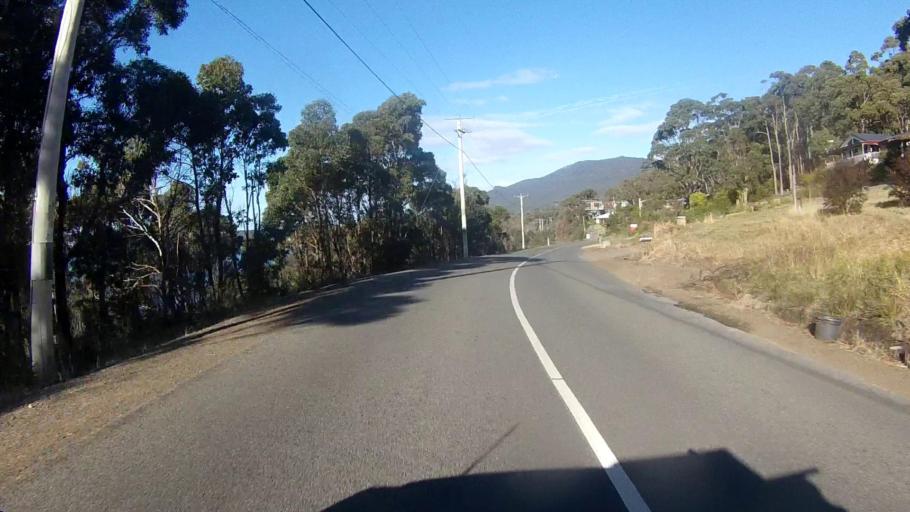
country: AU
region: Tasmania
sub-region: Clarence
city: Sandford
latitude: -43.0236
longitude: 147.9253
